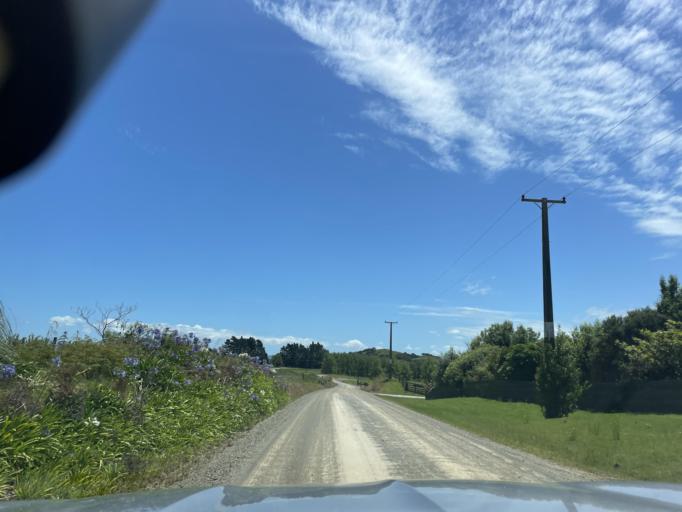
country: NZ
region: Auckland
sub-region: Auckland
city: Wellsford
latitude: -36.2255
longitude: 174.3699
